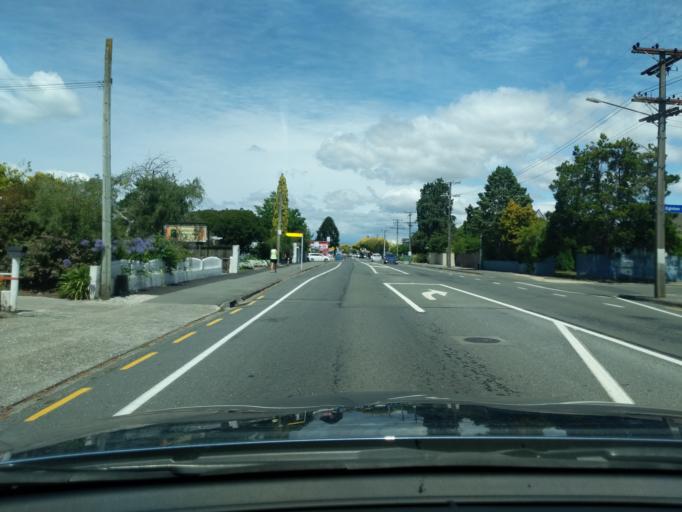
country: NZ
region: Tasman
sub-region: Tasman District
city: Motueka
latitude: -41.1063
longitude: 173.0114
